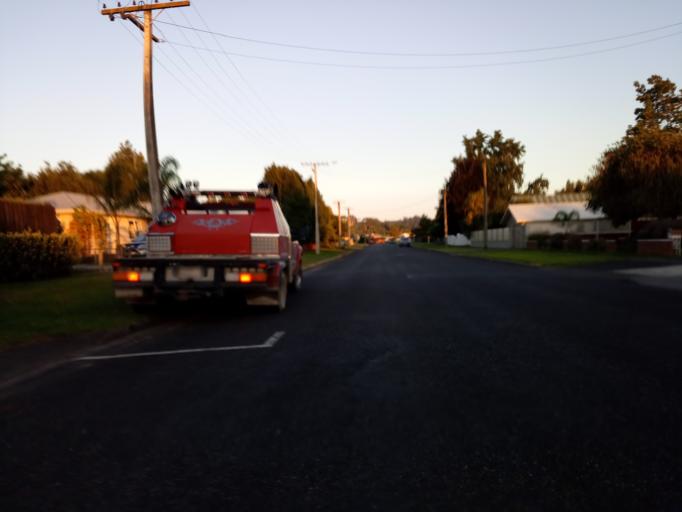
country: NZ
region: Gisborne
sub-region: Gisborne District
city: Gisborne
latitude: -38.6425
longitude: 178.0029
